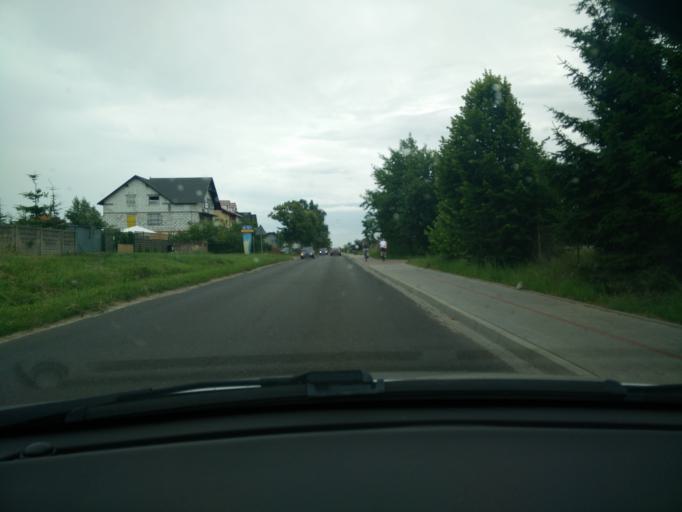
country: PL
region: Pomeranian Voivodeship
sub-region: Powiat pucki
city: Mosty
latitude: 54.6211
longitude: 18.4964
